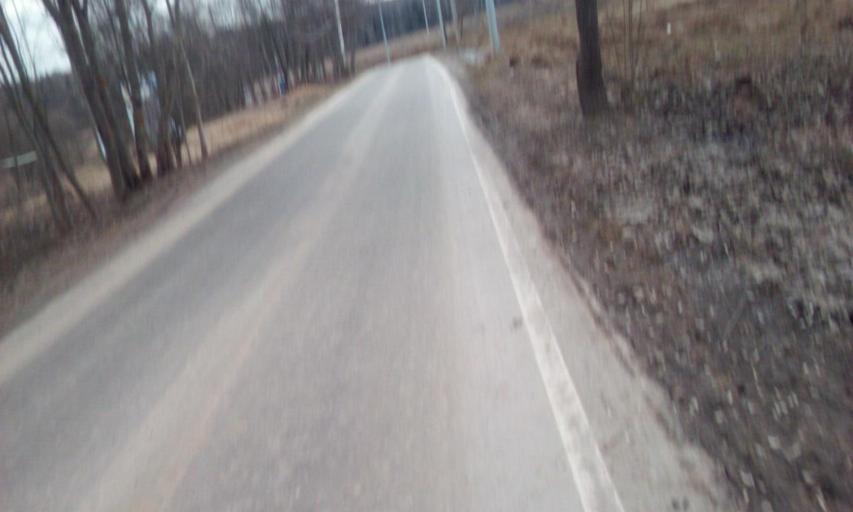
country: RU
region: Moskovskaya
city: Filimonki
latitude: 55.5277
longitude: 37.3576
